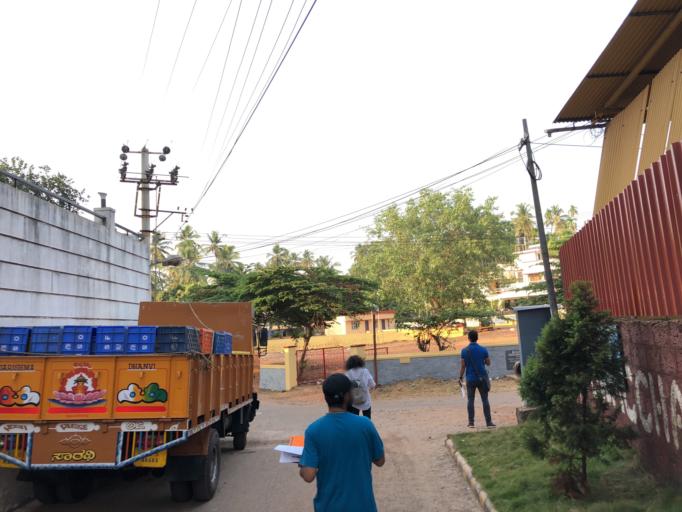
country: IN
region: Karnataka
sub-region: Dakshina Kannada
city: Mangalore
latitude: 12.8854
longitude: 74.8662
